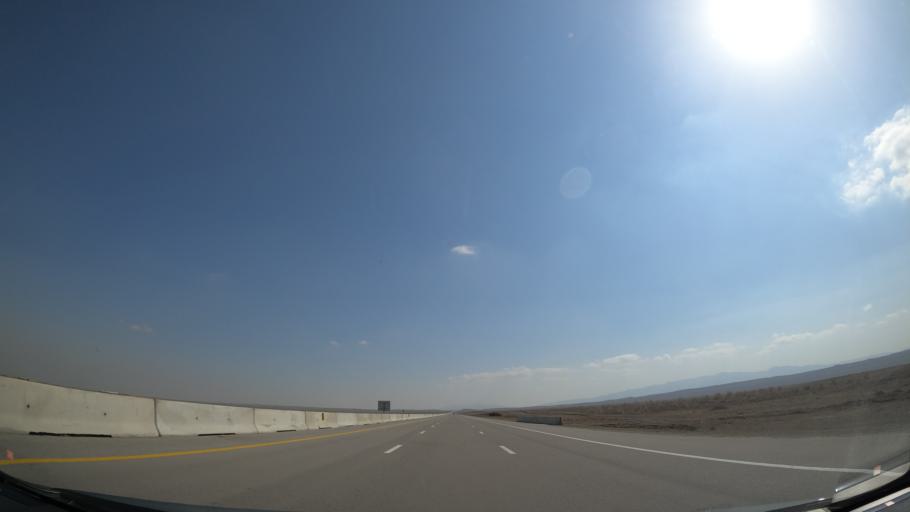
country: IR
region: Alborz
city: Nazarabad
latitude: 35.8278
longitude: 50.5041
